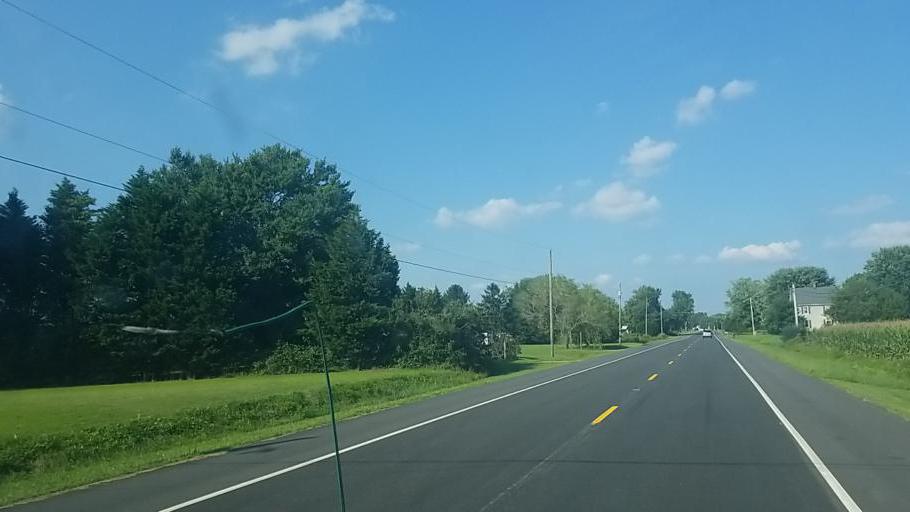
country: US
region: Maryland
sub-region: Worcester County
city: Berlin
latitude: 38.3600
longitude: -75.2095
